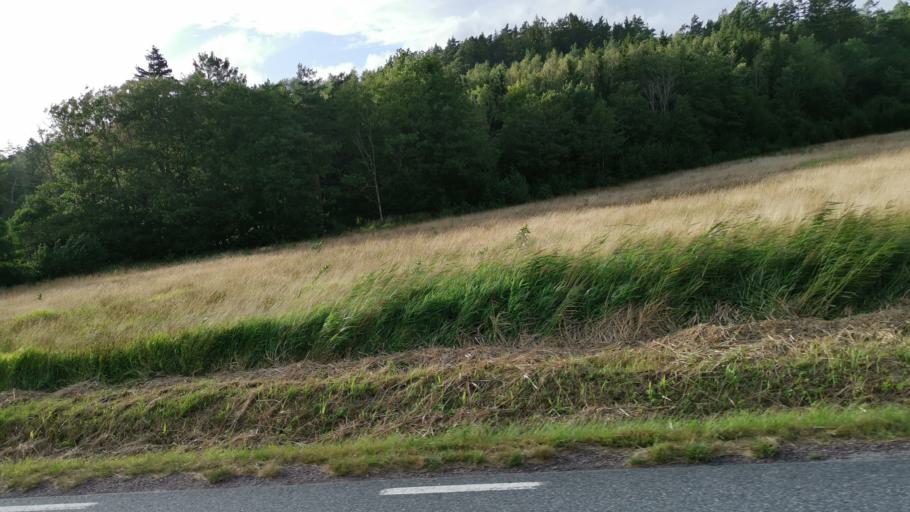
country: SE
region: Vaestra Goetaland
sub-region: Sotenas Kommun
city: Hunnebostrand
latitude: 58.4926
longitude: 11.3489
